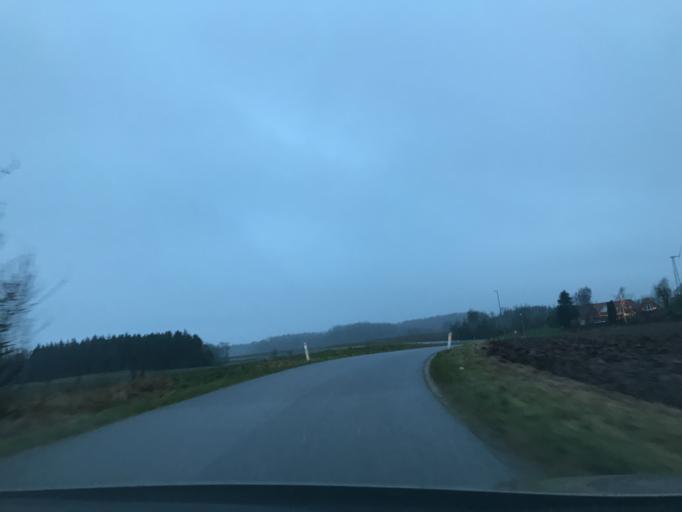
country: DK
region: South Denmark
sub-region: Vejle Kommune
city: Brejning
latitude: 55.6919
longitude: 9.7696
